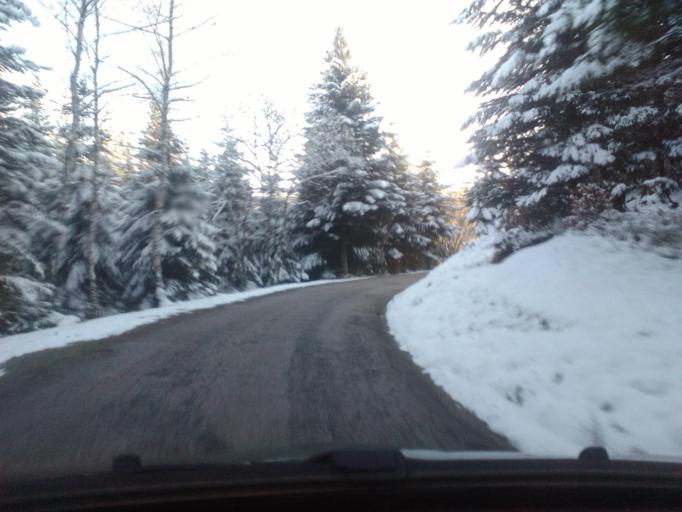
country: FR
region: Lorraine
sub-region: Departement des Vosges
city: Granges-sur-Vologne
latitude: 48.1387
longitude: 6.8289
